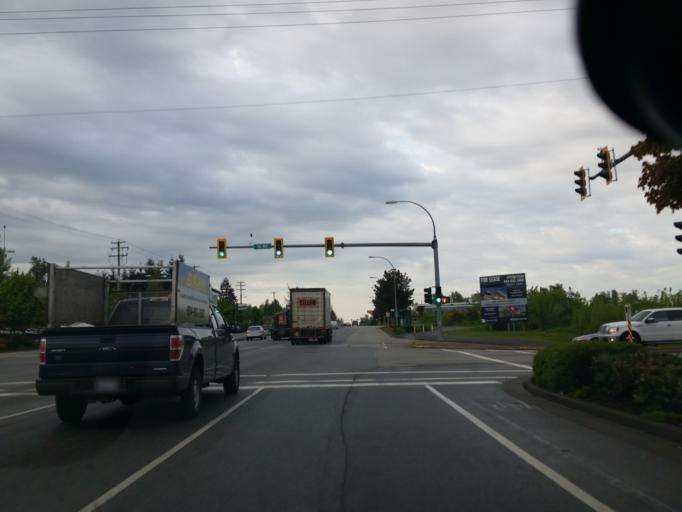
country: CA
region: British Columbia
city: Walnut Grove
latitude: 49.1596
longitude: -122.6681
